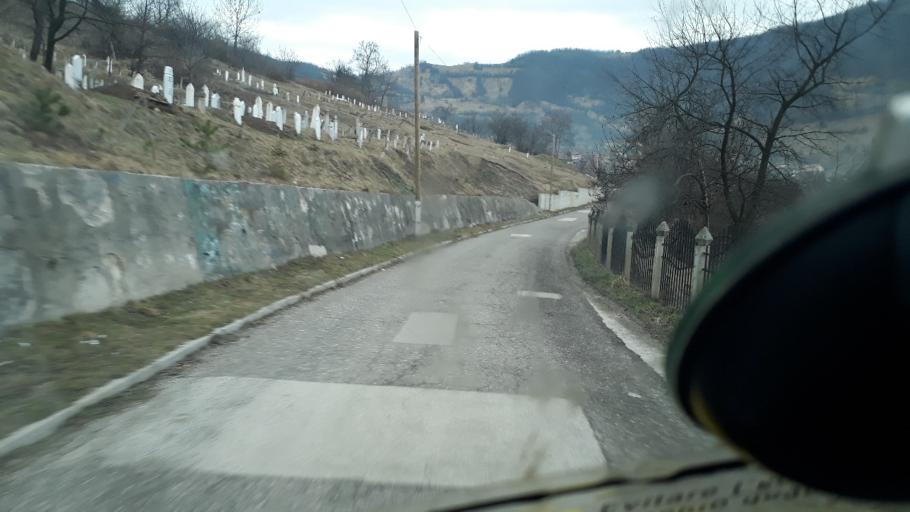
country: BA
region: Federation of Bosnia and Herzegovina
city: Zenica
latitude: 44.1560
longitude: 17.9695
